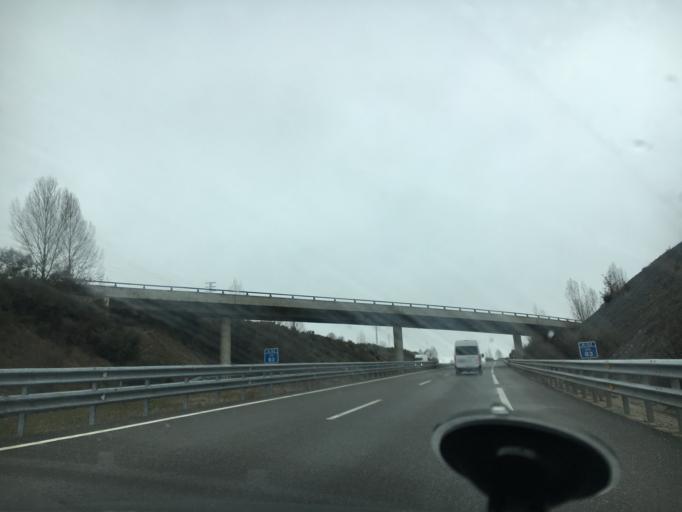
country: ES
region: Castille and Leon
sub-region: Provincia de Zamora
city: Puebla de Sanabria
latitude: 42.0624
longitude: -6.6479
